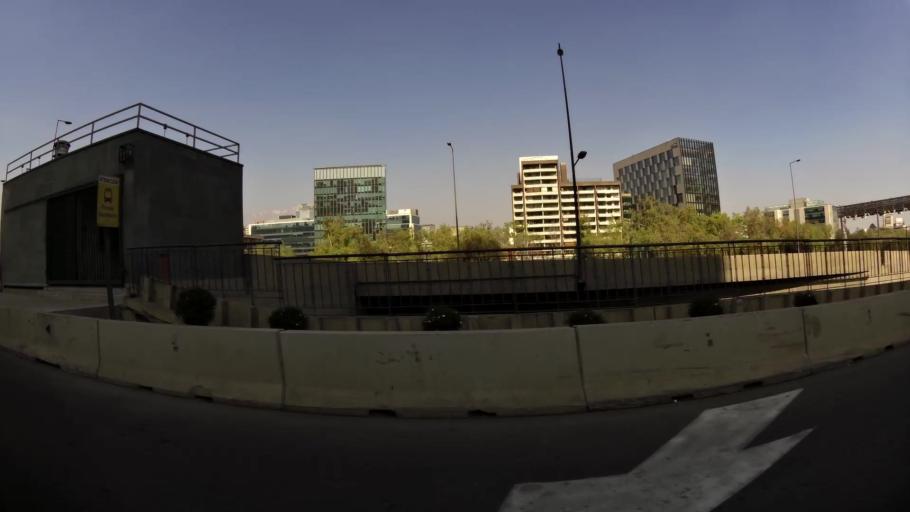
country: CL
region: Santiago Metropolitan
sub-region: Provincia de Santiago
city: Santiago
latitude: -33.4236
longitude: -70.6217
